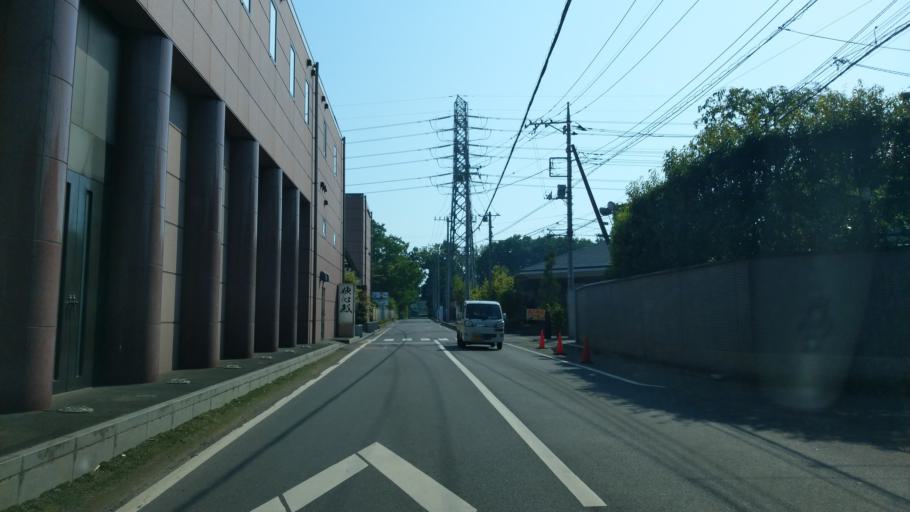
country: JP
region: Saitama
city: Oi
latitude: 35.8404
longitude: 139.4844
